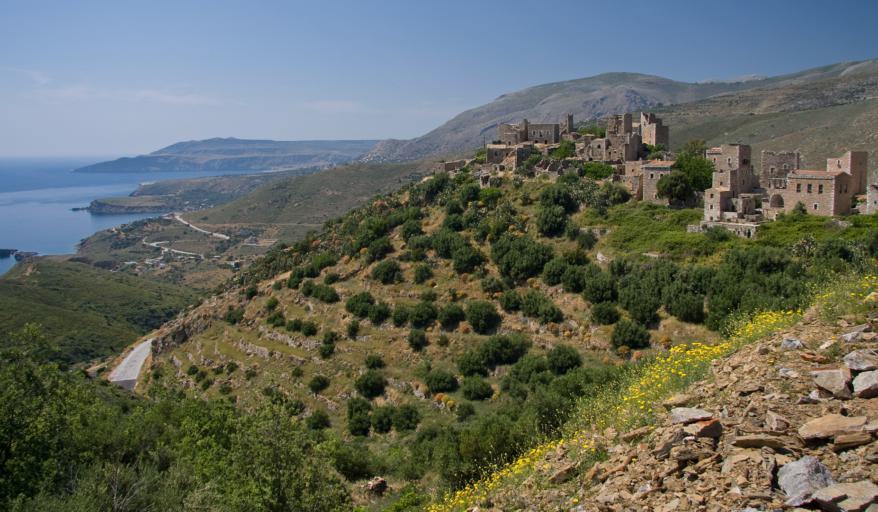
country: GR
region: Peloponnese
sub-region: Nomos Lakonias
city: Gytheio
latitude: 36.4517
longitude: 22.4674
